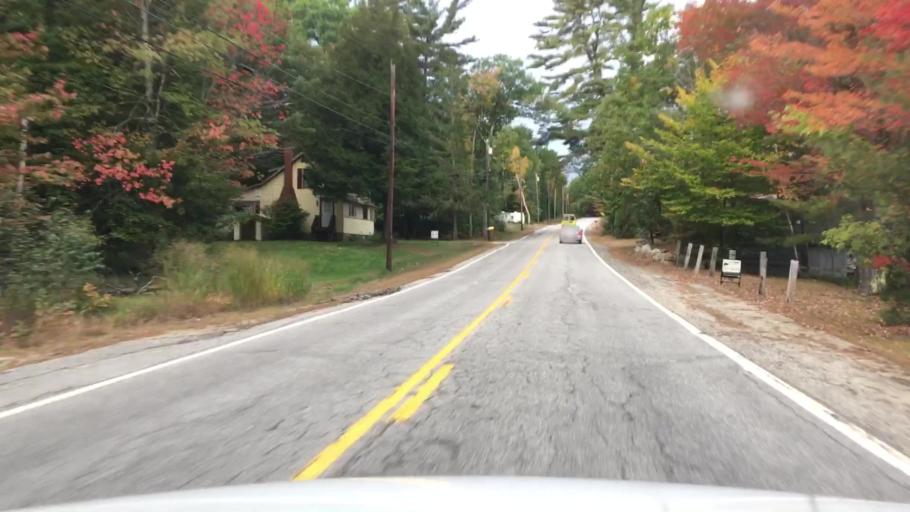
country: US
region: Maine
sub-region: Oxford County
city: Norway
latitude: 44.2236
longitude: -70.6222
